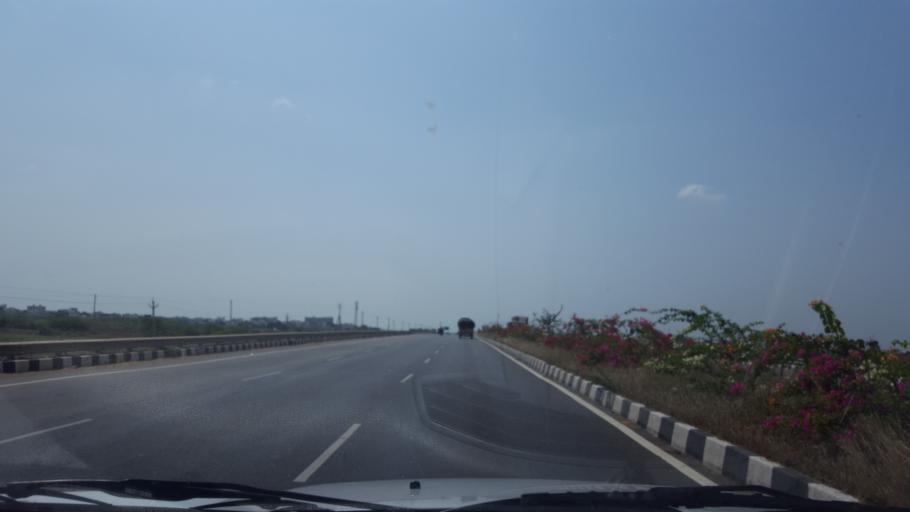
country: IN
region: Andhra Pradesh
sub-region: Prakasam
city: Ongole
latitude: 15.5064
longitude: 80.0723
